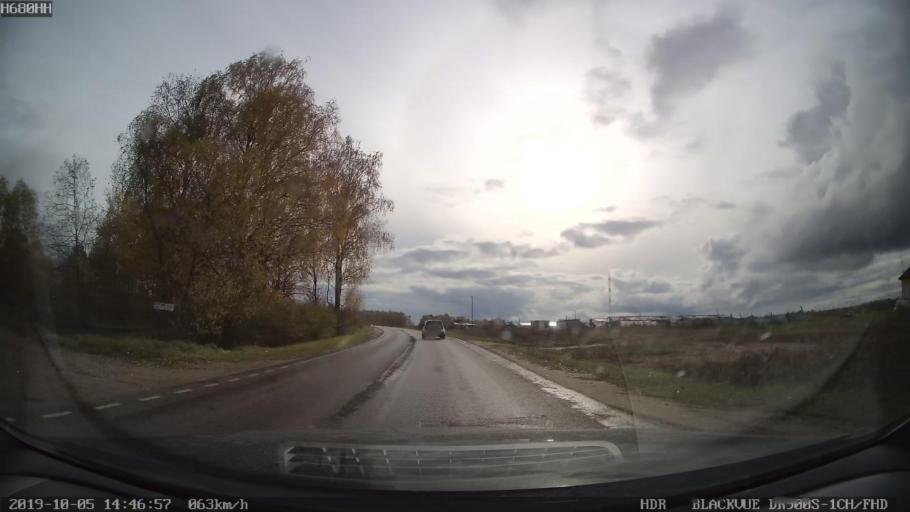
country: RU
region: Moskovskaya
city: Solnechnogorsk
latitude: 56.2226
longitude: 36.9050
